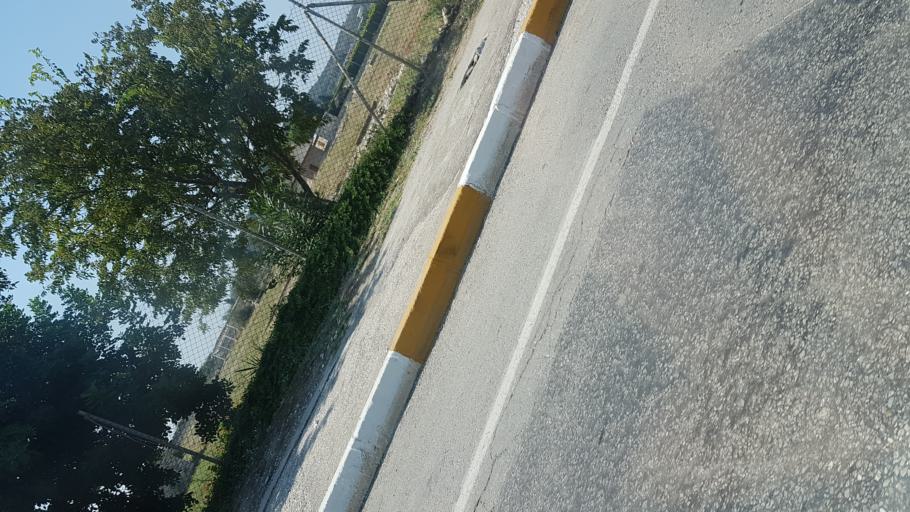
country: TR
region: Izmir
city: Urla
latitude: 38.3623
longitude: 26.7715
